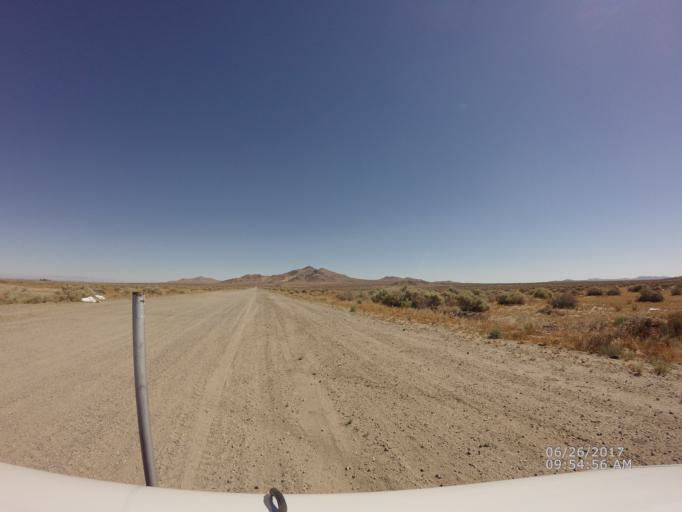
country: US
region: California
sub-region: Los Angeles County
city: Lake Los Angeles
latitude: 34.6347
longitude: -117.8094
